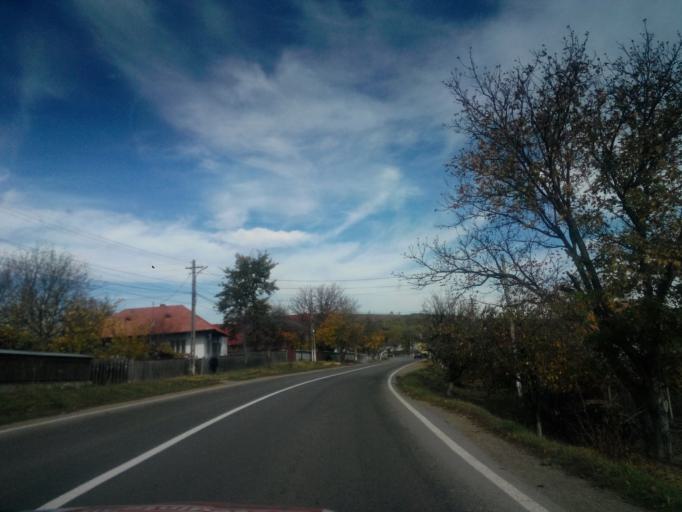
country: RO
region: Bacau
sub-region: Comuna Livezi
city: Orasa
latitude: 46.4198
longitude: 26.7409
